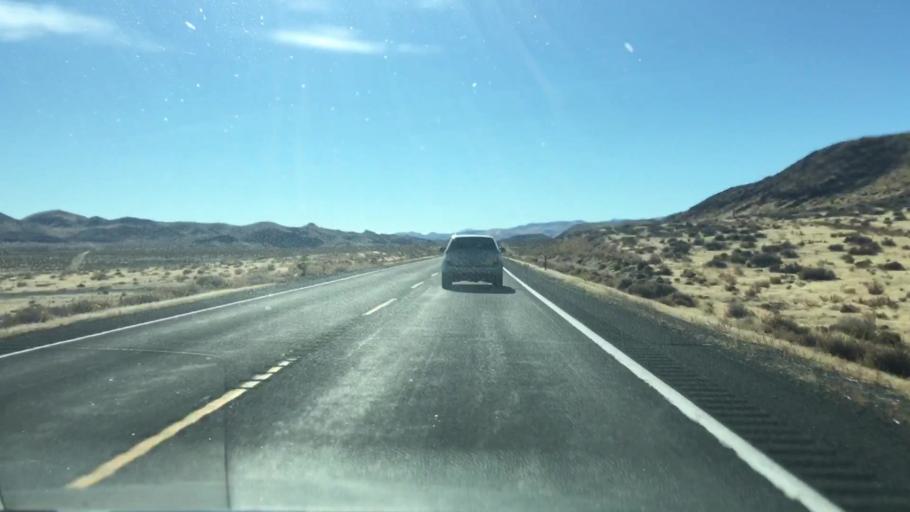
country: US
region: Nevada
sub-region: Lyon County
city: Silver Springs
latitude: 39.3167
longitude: -119.2502
